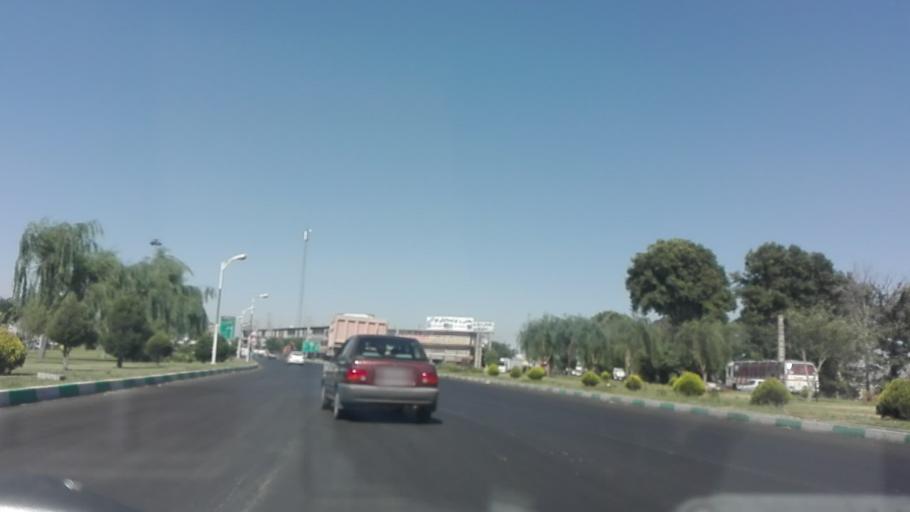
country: IR
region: Tehran
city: Malard
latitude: 35.6546
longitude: 51.0025
